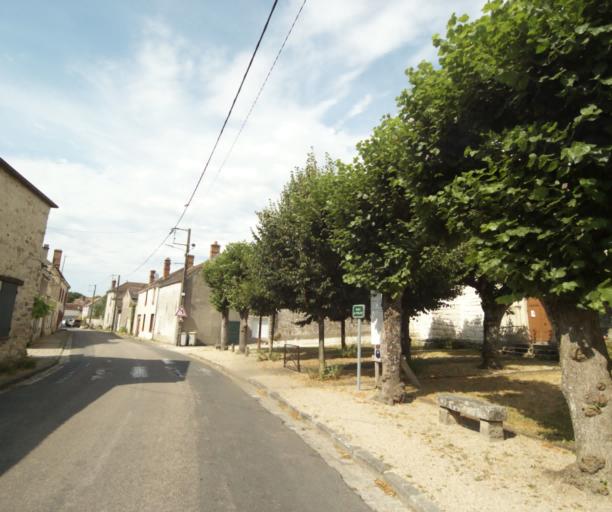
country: FR
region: Ile-de-France
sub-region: Departement de Seine-et-Marne
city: Acheres-la-Foret
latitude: 48.3543
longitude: 2.5704
